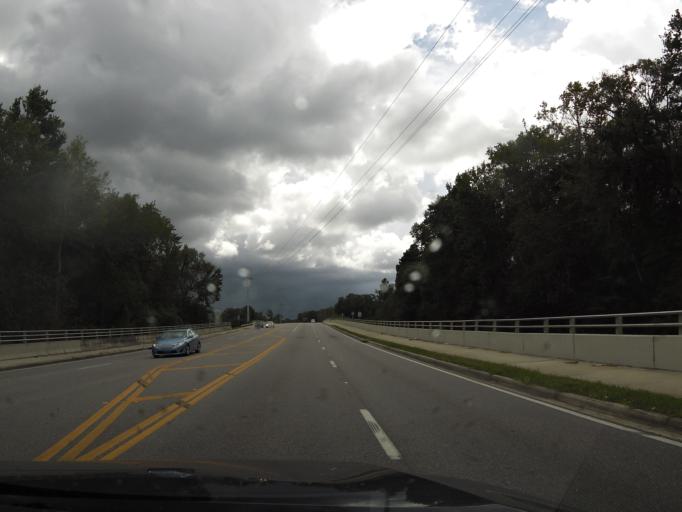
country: US
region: Florida
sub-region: Clay County
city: Asbury Lake
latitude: 30.0842
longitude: -81.8095
